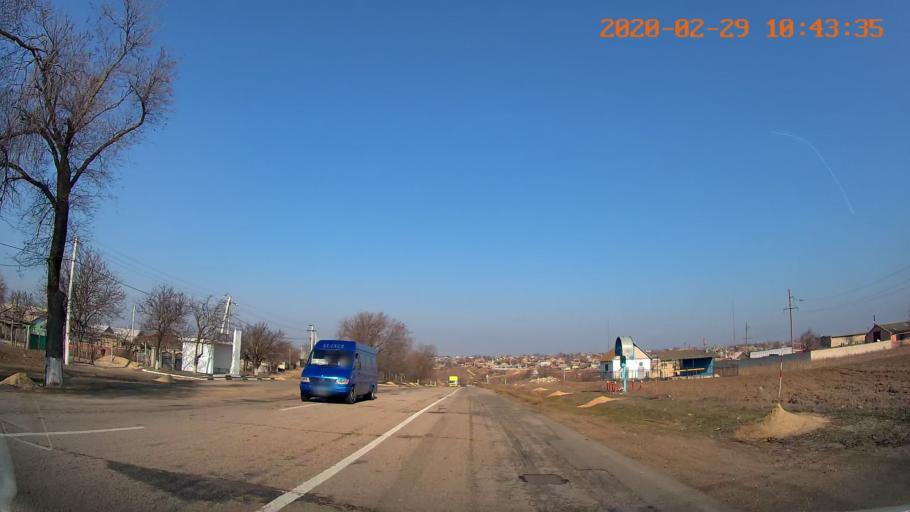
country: MD
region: Telenesti
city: Grigoriopol
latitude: 47.0630
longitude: 29.4027
